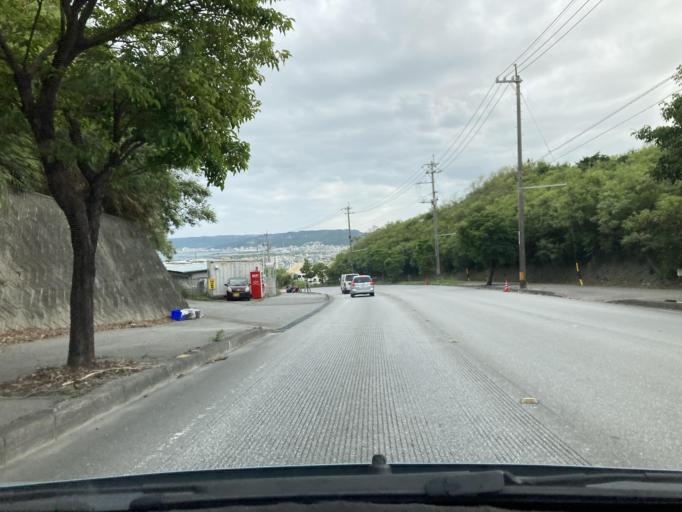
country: JP
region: Okinawa
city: Ginowan
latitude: 26.2361
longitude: 127.7663
